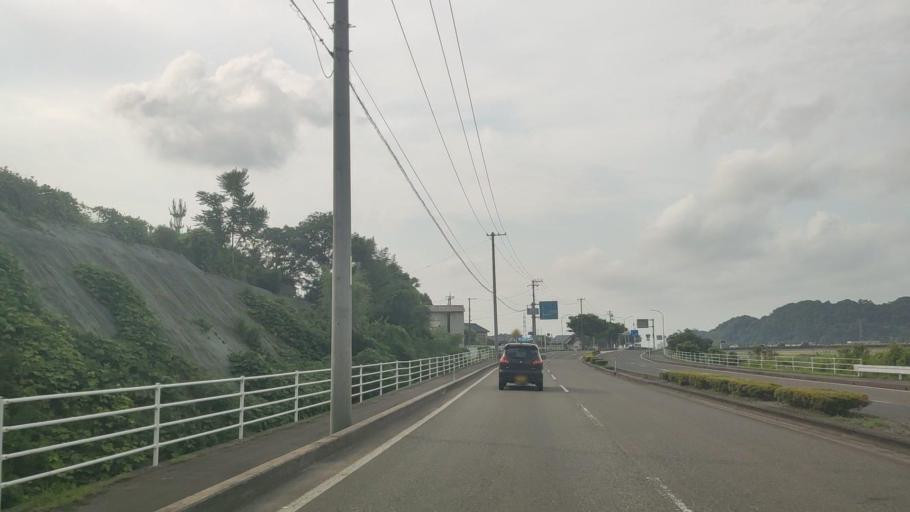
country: JP
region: Tottori
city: Kurayoshi
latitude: 35.4205
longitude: 133.8498
